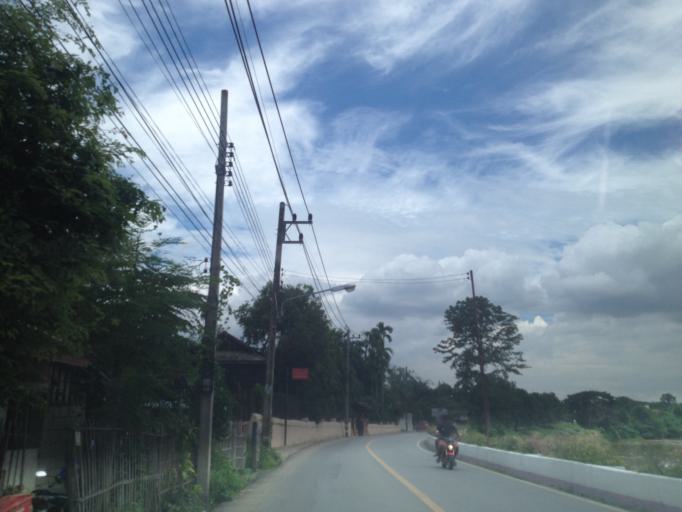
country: TH
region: Chiang Mai
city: Saraphi
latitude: 18.7287
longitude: 98.9849
